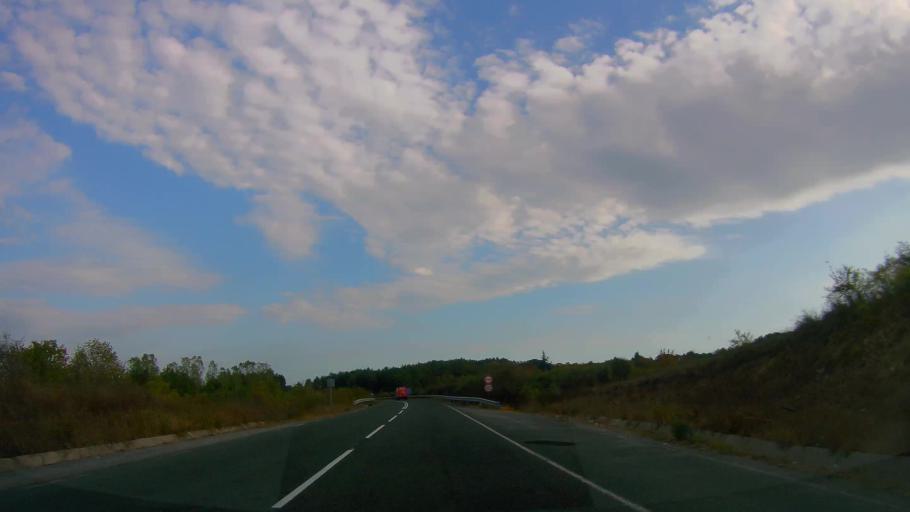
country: BG
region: Burgas
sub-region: Obshtina Sozopol
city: Sozopol
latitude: 42.4019
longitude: 27.6758
